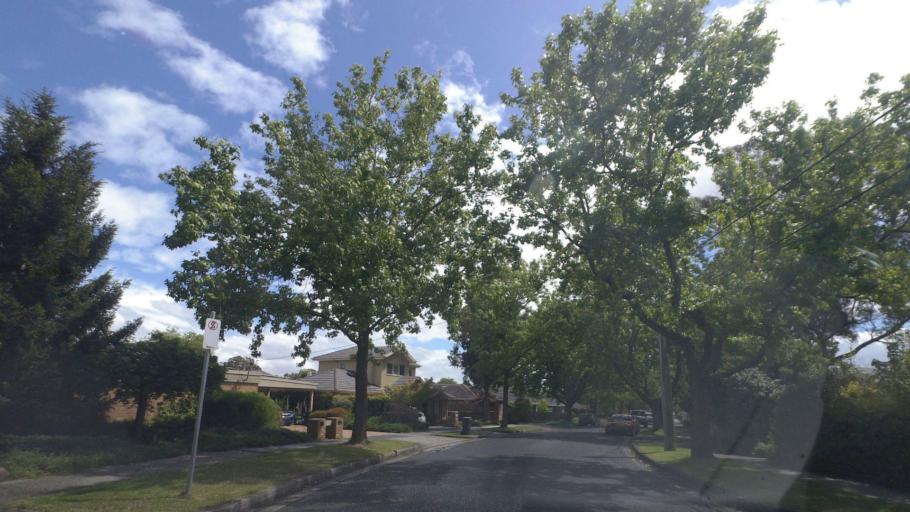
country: AU
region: Victoria
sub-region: Whitehorse
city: Vermont
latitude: -37.8269
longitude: 145.1925
